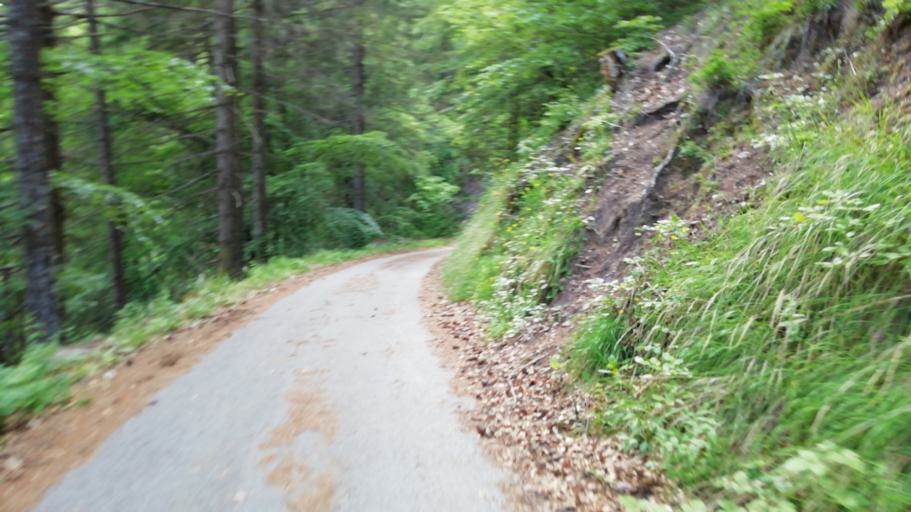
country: IT
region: Veneto
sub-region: Provincia di Belluno
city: Valle di Cadore
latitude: 46.4231
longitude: 12.3235
